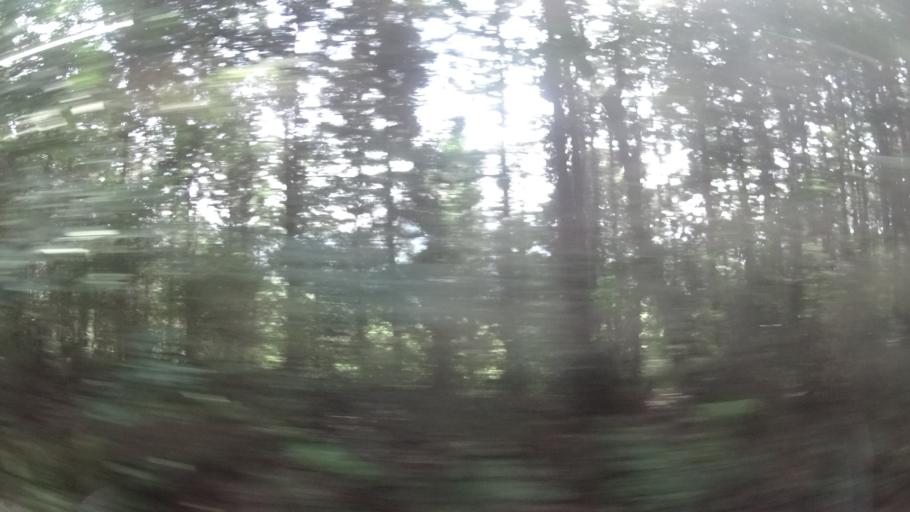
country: JP
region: Tochigi
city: Kanuma
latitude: 36.6253
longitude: 139.7315
